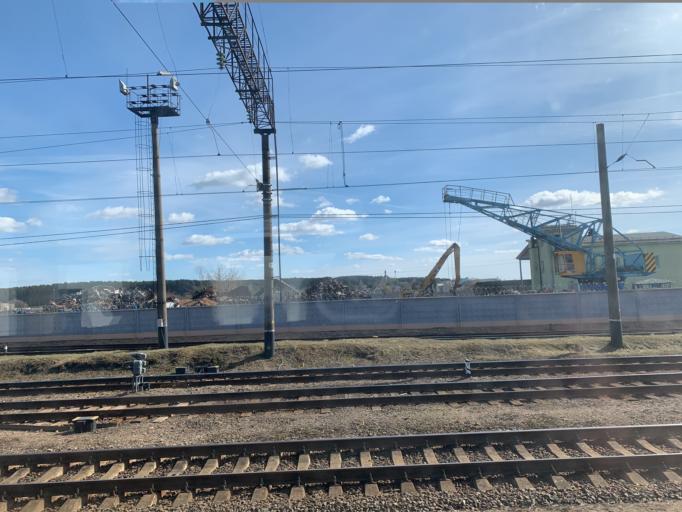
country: BY
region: Minsk
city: Stowbtsy
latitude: 53.4802
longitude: 26.7526
